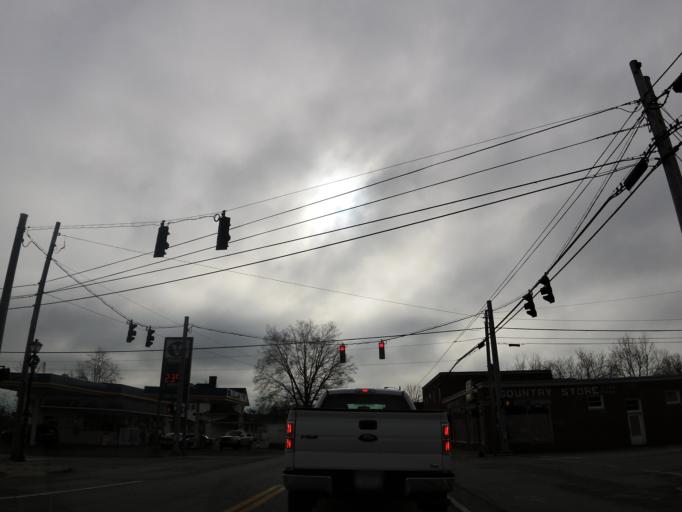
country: US
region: Kentucky
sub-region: Trimble County
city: Bedford
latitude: 38.5930
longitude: -85.3176
